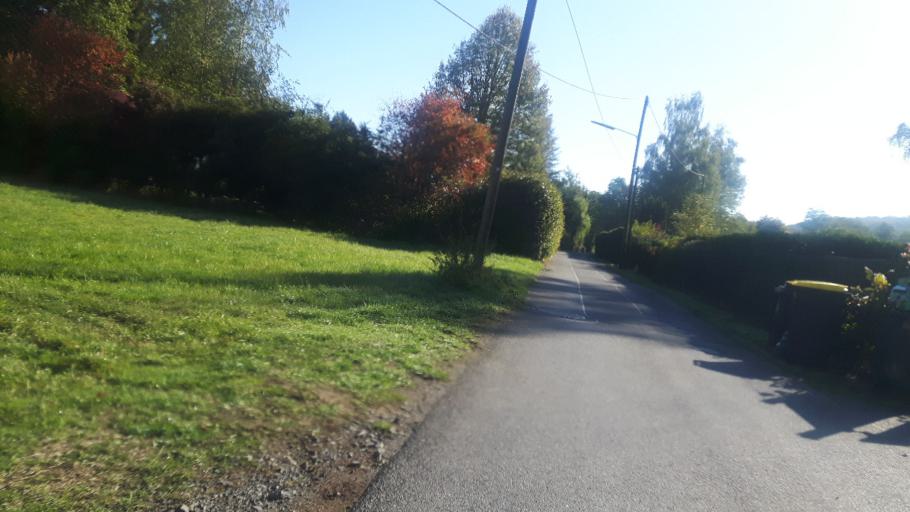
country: DE
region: Rheinland-Pfalz
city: Niederirsen
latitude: 50.7986
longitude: 7.5580
